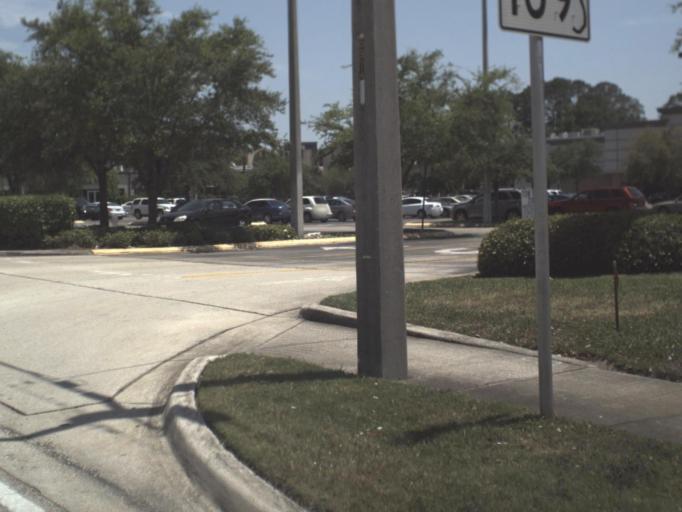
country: US
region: Florida
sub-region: Duval County
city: Jacksonville
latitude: 30.2929
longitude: -81.6035
